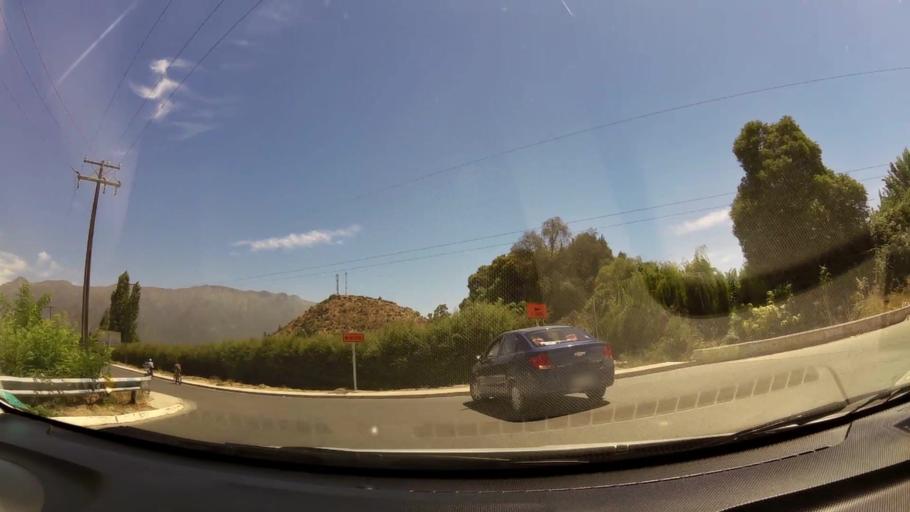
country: CL
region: O'Higgins
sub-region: Provincia de Cachapoal
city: Graneros
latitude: -34.0589
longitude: -70.7201
